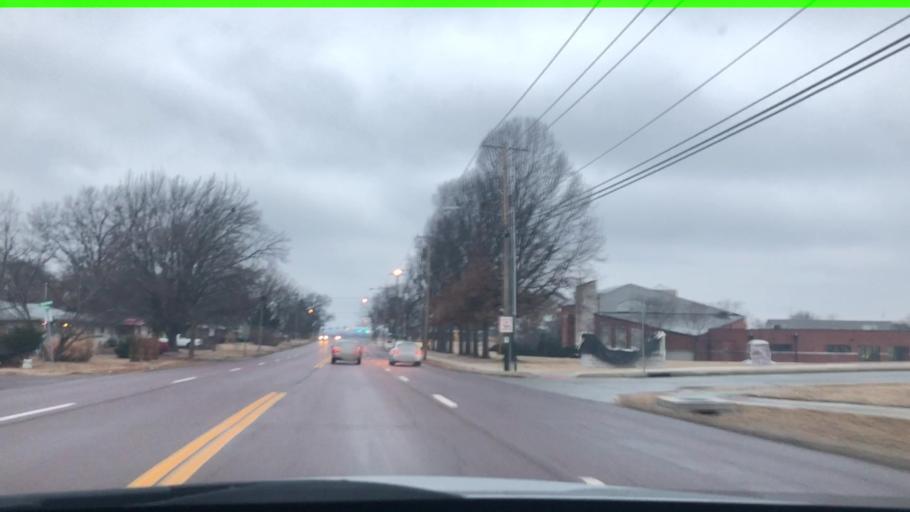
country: US
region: Missouri
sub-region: Boone County
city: Columbia
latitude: 38.9543
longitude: -92.3758
